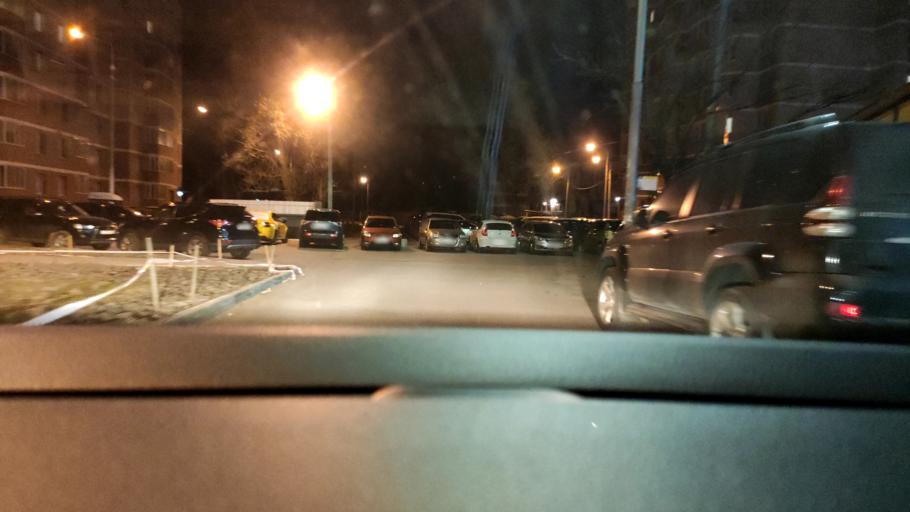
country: RU
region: Moskovskaya
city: Reutov
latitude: 55.7753
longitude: 37.8936
